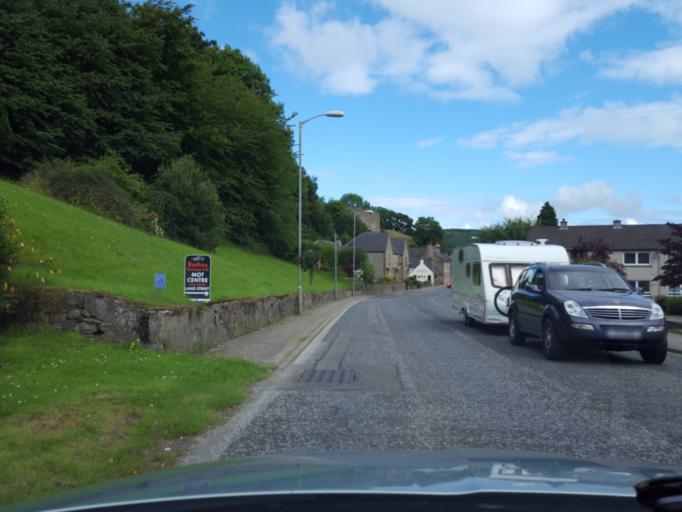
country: GB
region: Scotland
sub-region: Moray
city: Rothes
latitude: 57.5224
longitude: -3.2086
